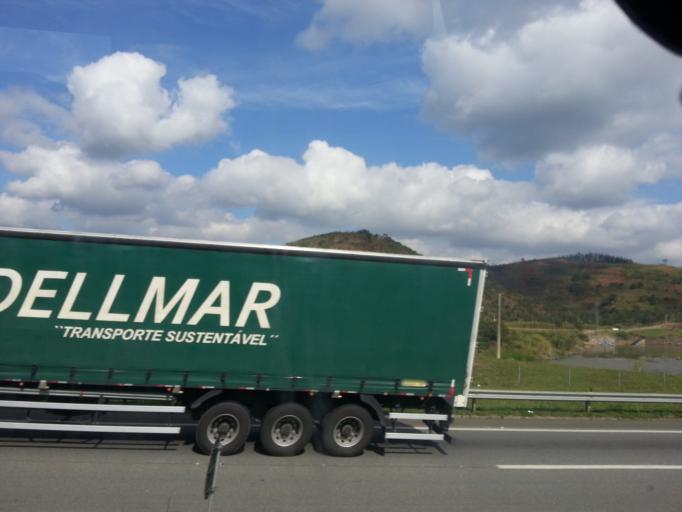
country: BR
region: Sao Paulo
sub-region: Cruzeiro
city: Cruzeiro
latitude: -22.5432
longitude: -44.7913
